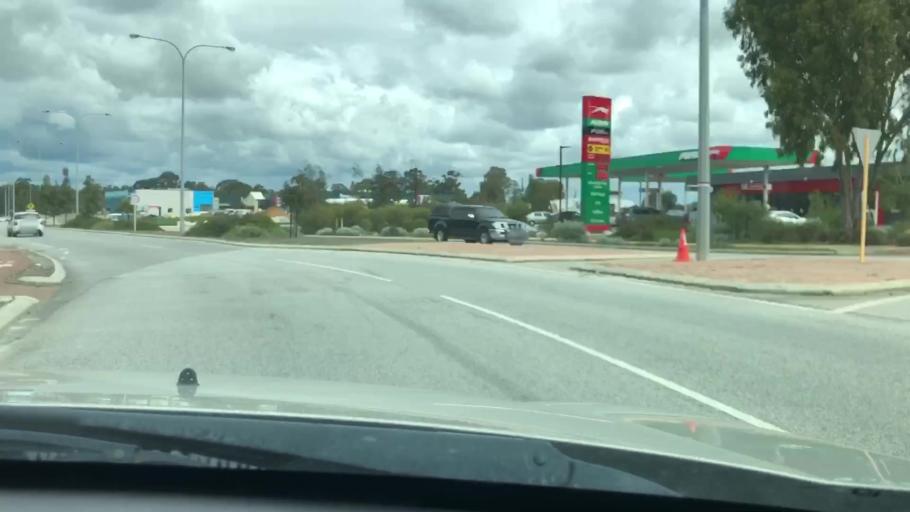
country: AU
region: Western Australia
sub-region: Armadale
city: Seville Grove
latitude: -32.1429
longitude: 115.9760
